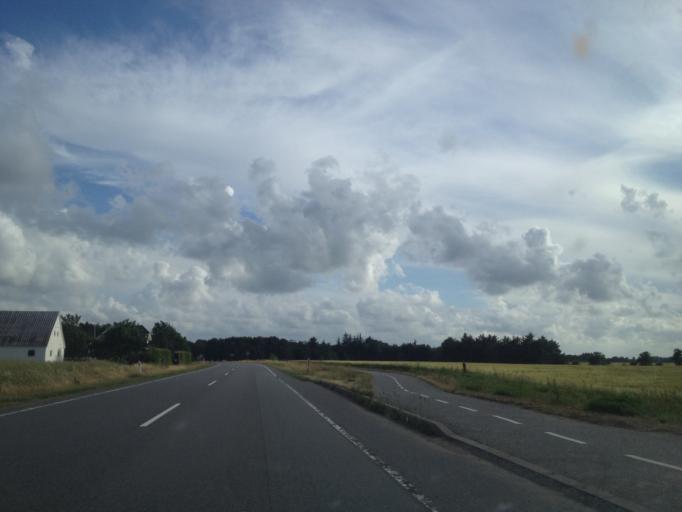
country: DK
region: South Denmark
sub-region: Vejen Kommune
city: Brorup
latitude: 55.4465
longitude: 9.0057
